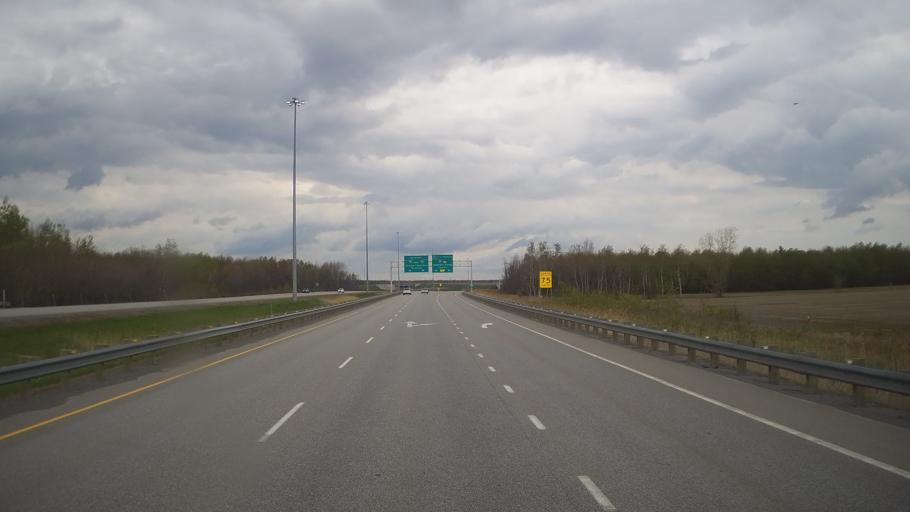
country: CA
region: Quebec
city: Les Cedres
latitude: 45.3457
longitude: -74.0434
